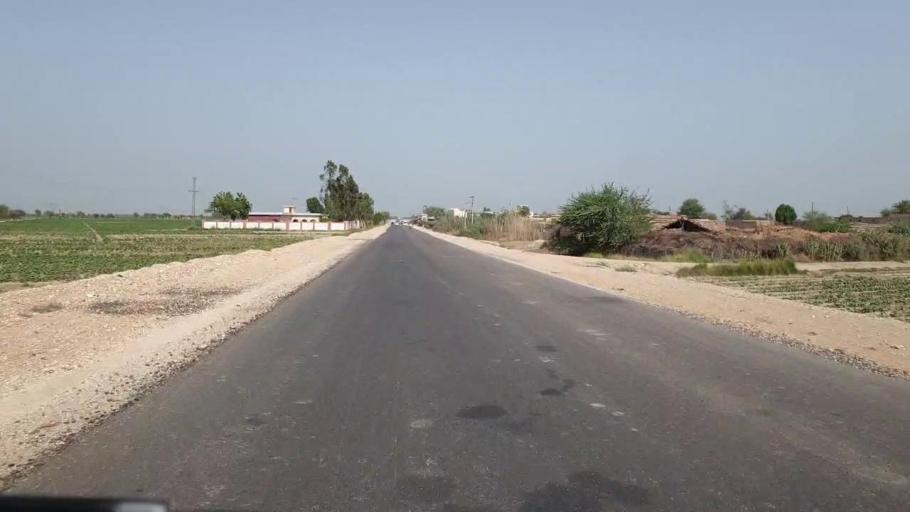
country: PK
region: Sindh
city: Sakrand
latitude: 26.2645
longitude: 68.1759
